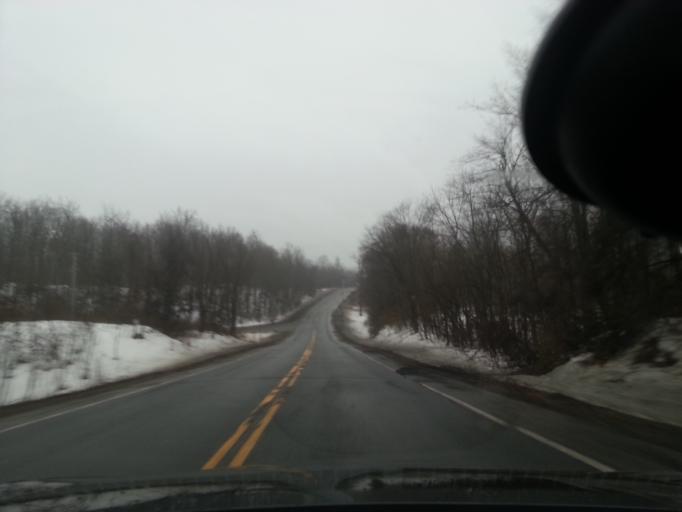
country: US
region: New York
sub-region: St. Lawrence County
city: Canton
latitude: 44.5195
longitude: -75.3379
